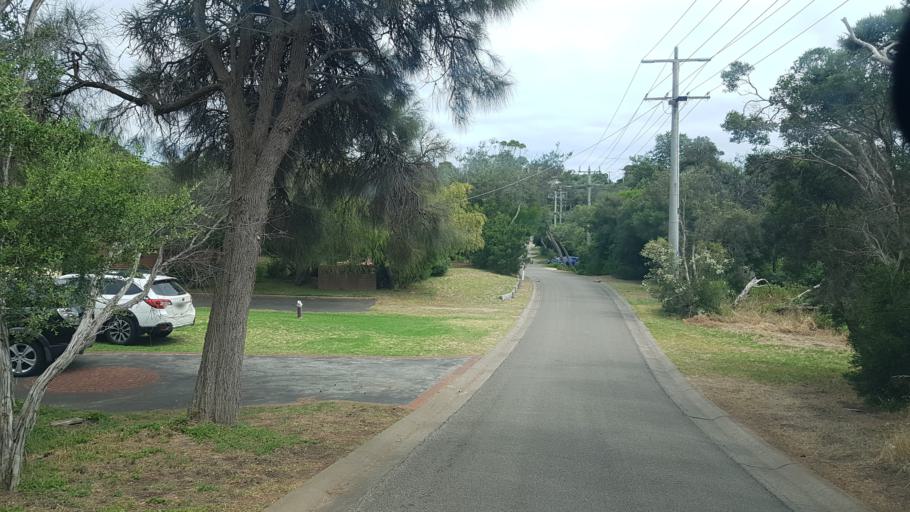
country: AU
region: Victoria
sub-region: Mornington Peninsula
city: Blairgowrie
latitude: -38.3677
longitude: 144.7754
